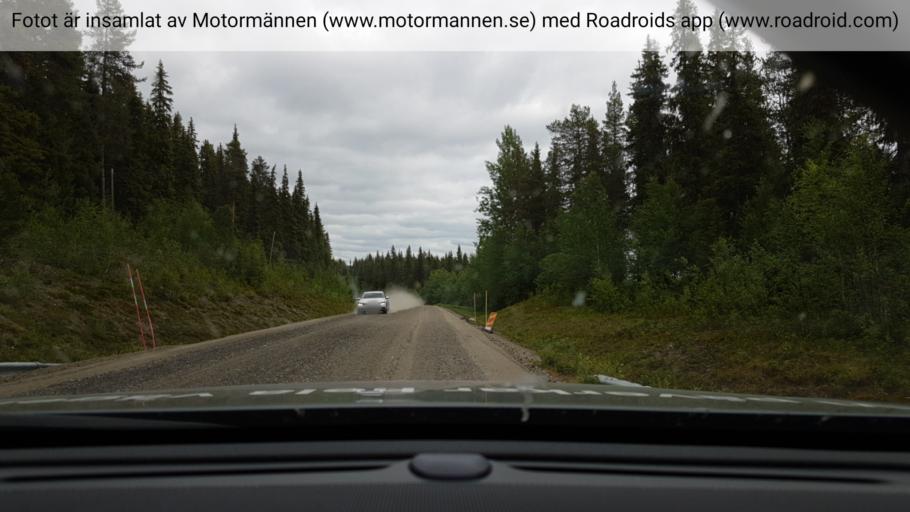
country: SE
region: Vaesterbotten
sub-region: Storumans Kommun
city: Fristad
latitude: 65.8184
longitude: 16.8009
